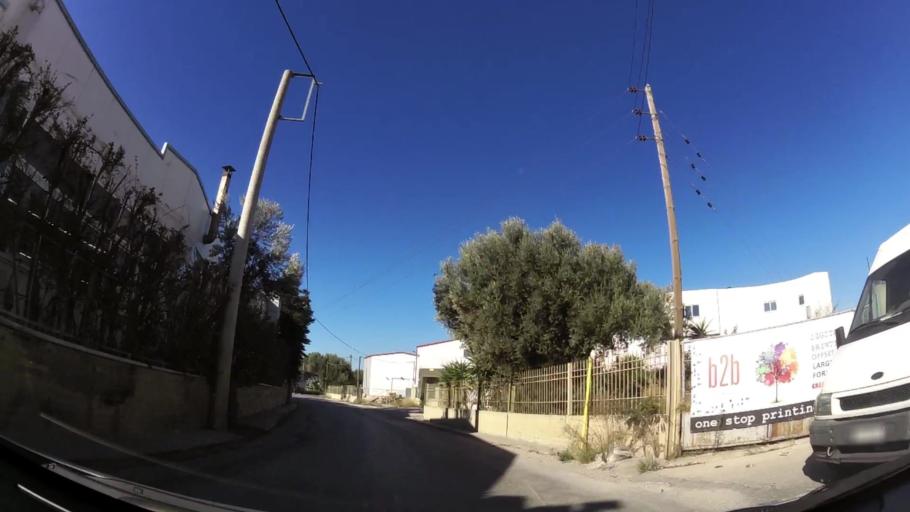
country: GR
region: Attica
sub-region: Nomarchia Athinas
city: Metamorfosi
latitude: 38.0790
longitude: 23.7580
